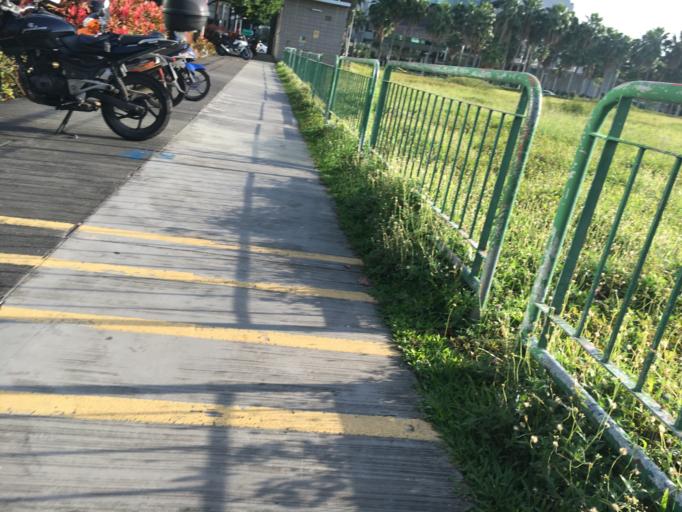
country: SG
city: Singapore
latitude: 1.2815
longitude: 103.8590
